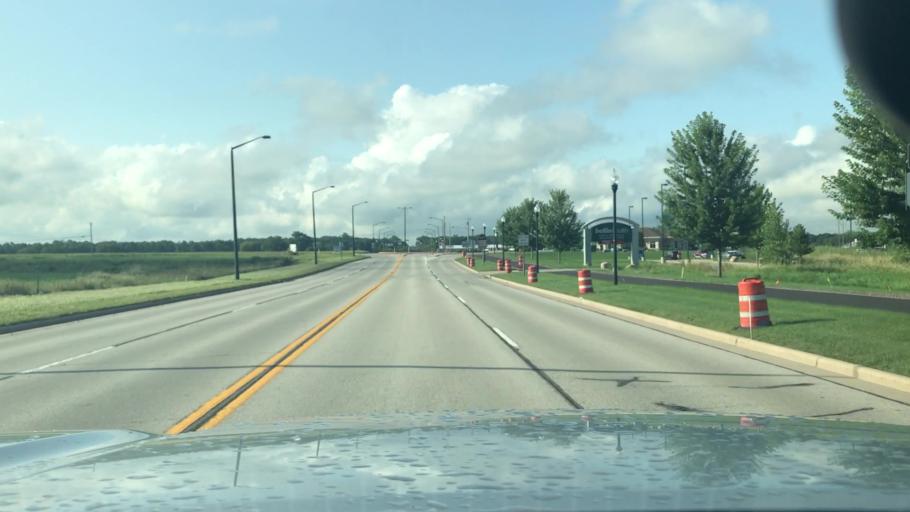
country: US
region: Wisconsin
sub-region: Brown County
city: Bellevue
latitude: 44.4680
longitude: -87.9173
